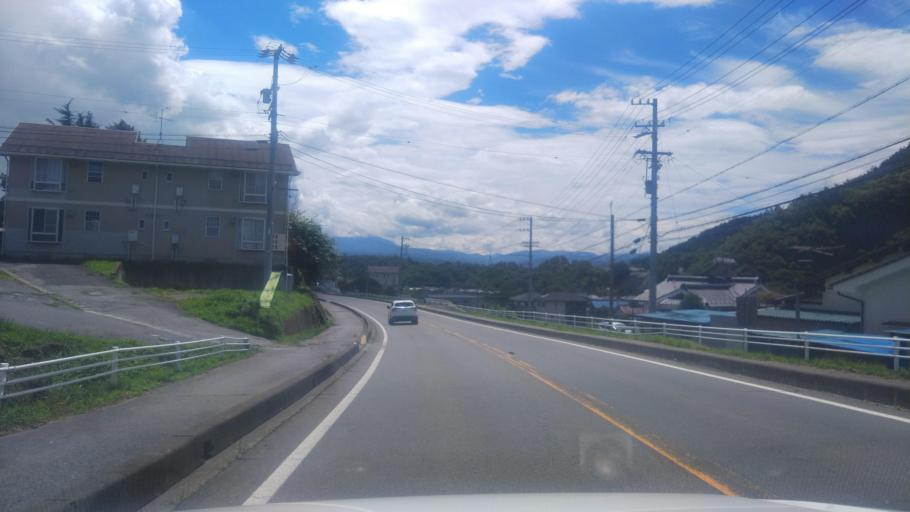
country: JP
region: Nagano
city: Ueda
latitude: 36.4287
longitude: 138.2981
